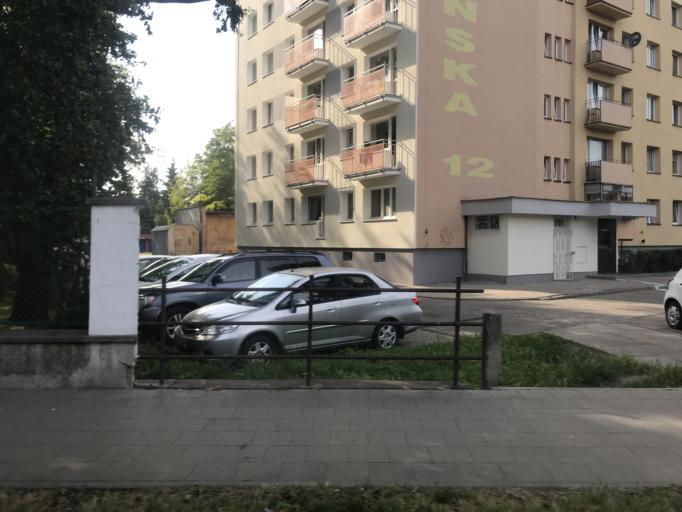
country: PL
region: Pomeranian Voivodeship
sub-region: Gdansk
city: Gdansk
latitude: 54.4051
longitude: 18.6352
